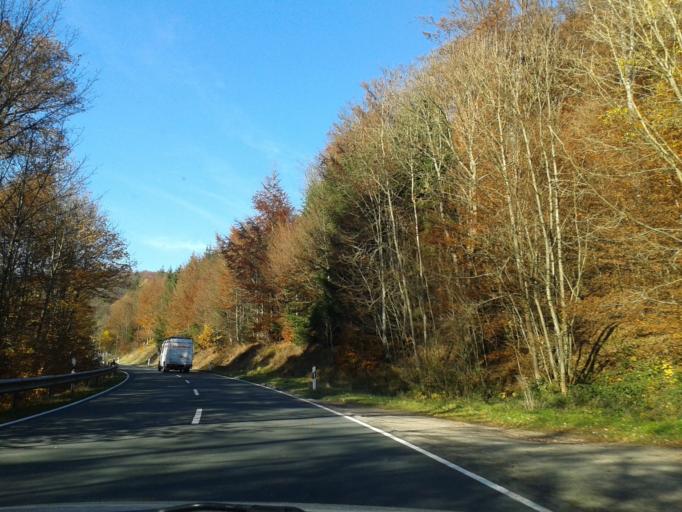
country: DE
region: North Rhine-Westphalia
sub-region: Regierungsbezirk Arnsberg
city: Erndtebruck
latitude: 50.9720
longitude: 8.3397
